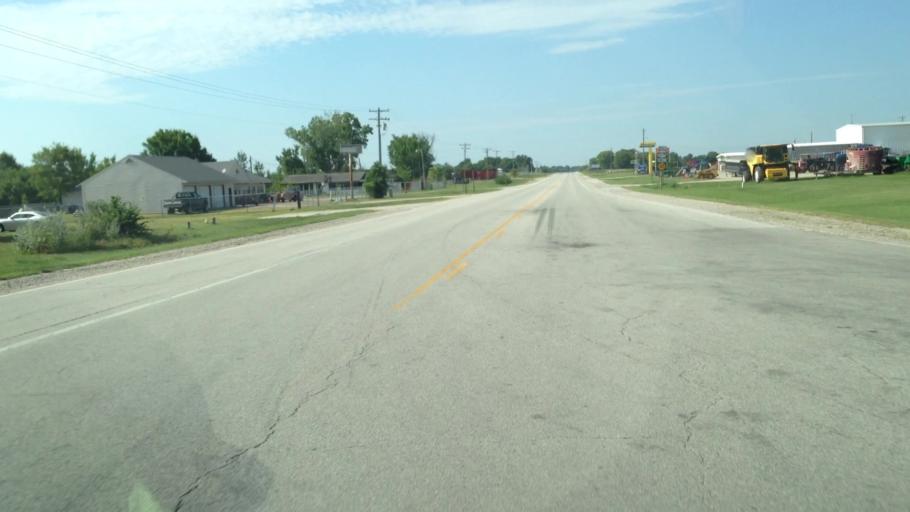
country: US
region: Kansas
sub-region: Neosho County
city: Erie
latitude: 37.5157
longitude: -95.2699
